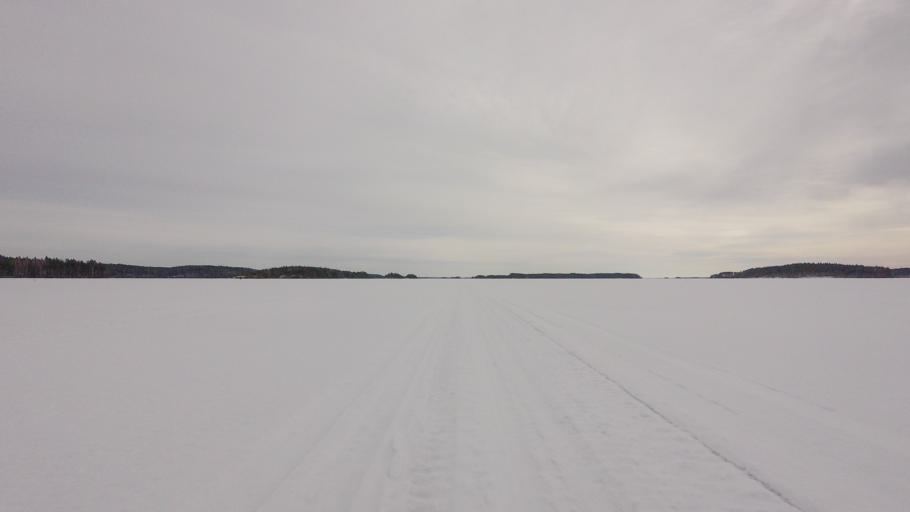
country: FI
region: Southern Savonia
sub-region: Savonlinna
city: Rantasalmi
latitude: 62.0994
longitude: 28.4719
